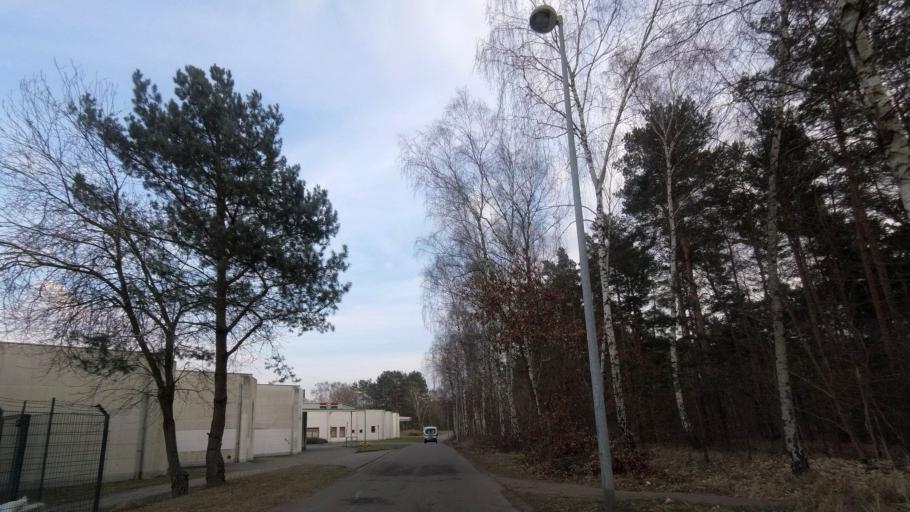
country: DE
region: Brandenburg
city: Belzig
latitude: 52.1433
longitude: 12.6114
